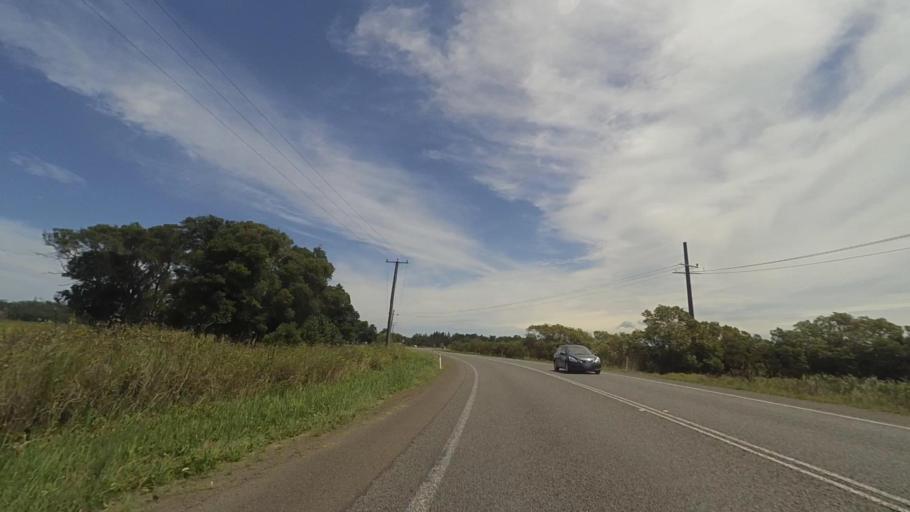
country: AU
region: New South Wales
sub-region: Port Stephens Shire
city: Medowie
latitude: -32.7867
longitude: 151.9226
